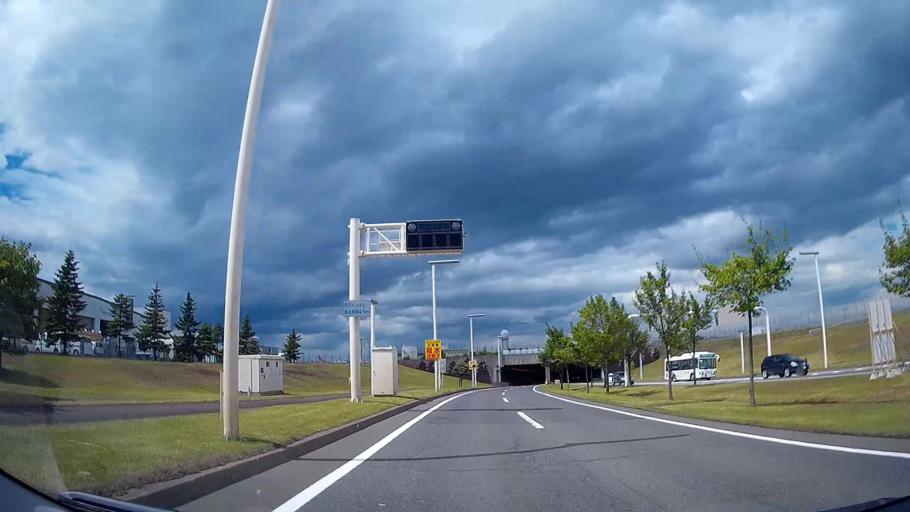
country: JP
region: Hokkaido
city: Chitose
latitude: 42.7893
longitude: 141.6763
